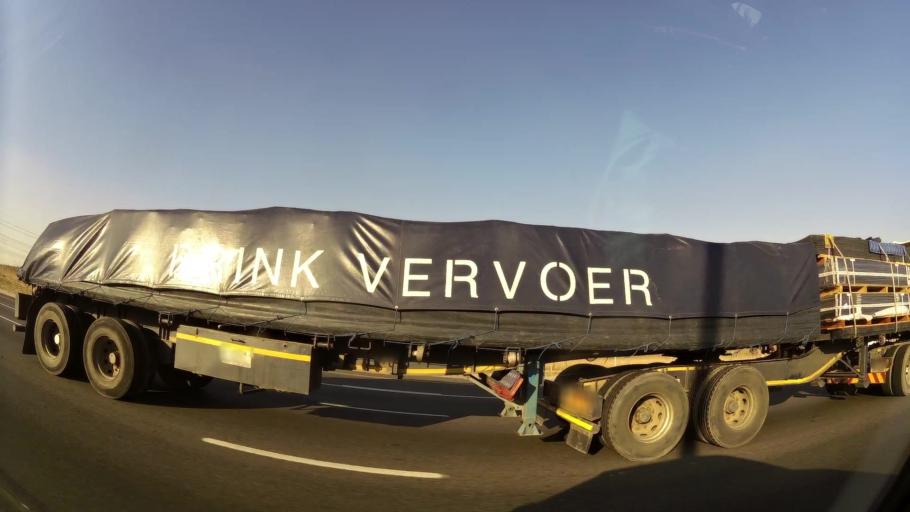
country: ZA
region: Gauteng
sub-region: Ekurhuleni Metropolitan Municipality
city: Germiston
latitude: -26.2307
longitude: 28.1259
